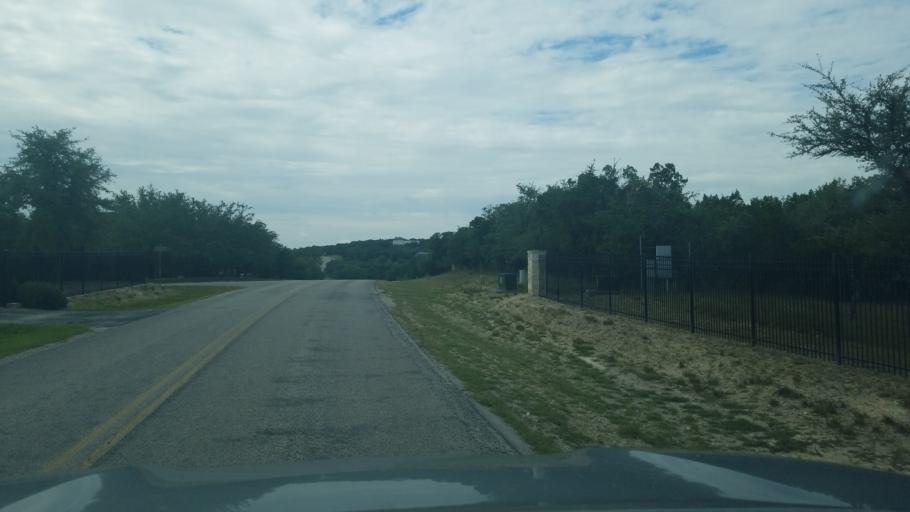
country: US
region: Texas
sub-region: Comal County
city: Bulverde
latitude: 29.8261
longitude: -98.4072
